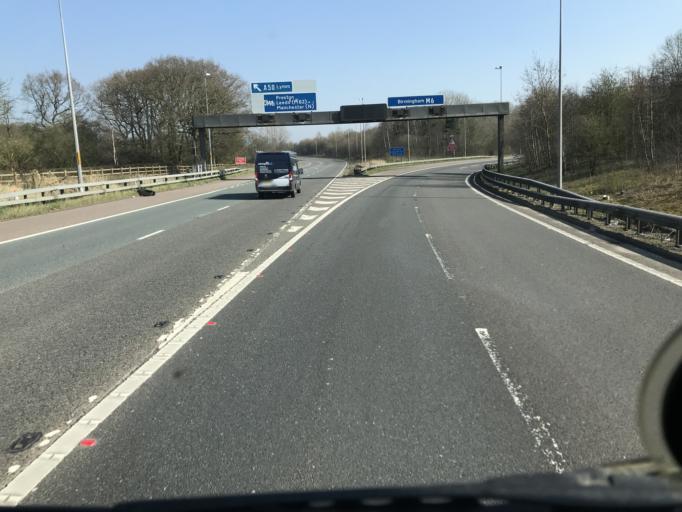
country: GB
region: England
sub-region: Warrington
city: Appleton Thorn
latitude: 53.3515
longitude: -2.5107
